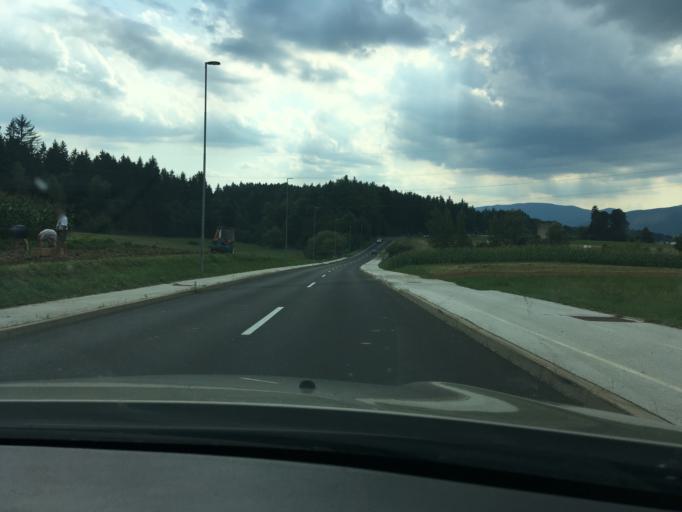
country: SI
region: Novo Mesto
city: Novo Mesto
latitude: 45.7946
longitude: 15.1441
